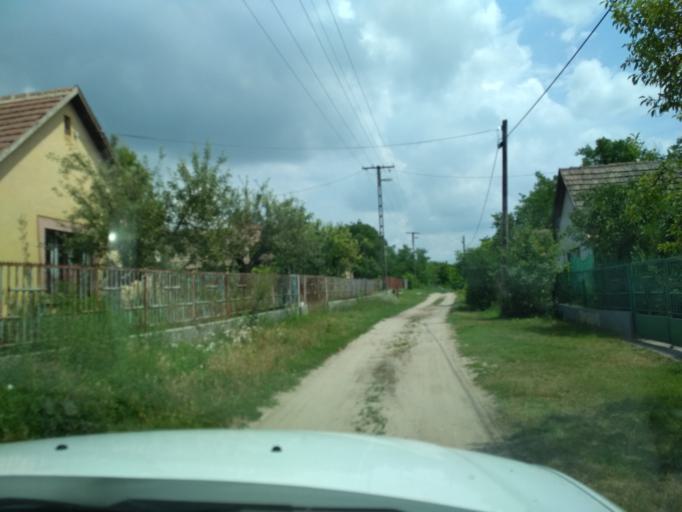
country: HU
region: Pest
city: Tapioszentmarton
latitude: 47.3679
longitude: 19.7682
